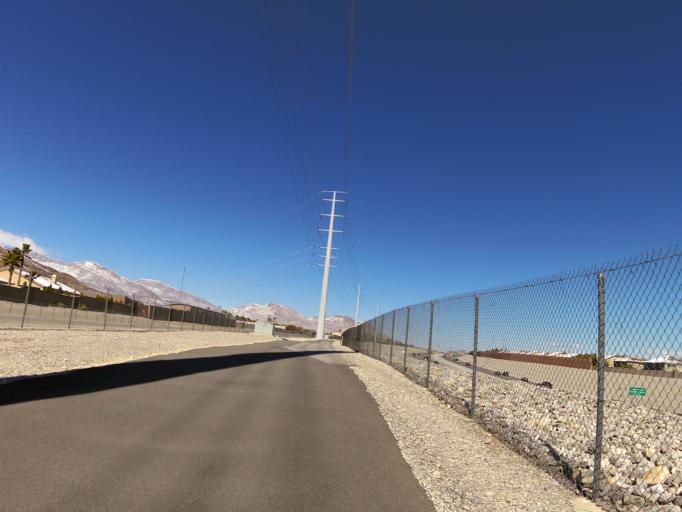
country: US
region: Nevada
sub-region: Clark County
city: Summerlin South
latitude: 36.1303
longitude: -115.3359
